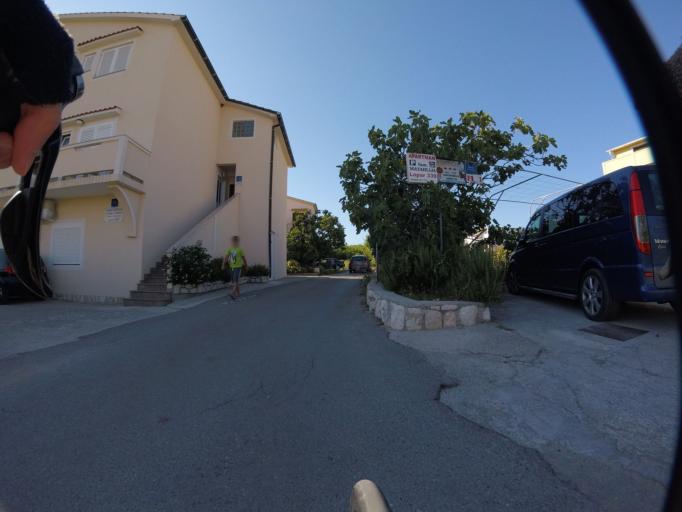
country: HR
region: Primorsko-Goranska
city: Lopar
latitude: 44.8316
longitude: 14.7319
